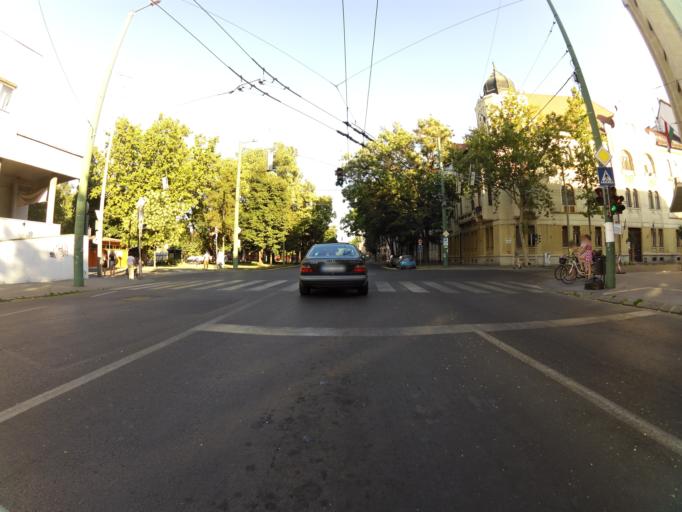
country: HU
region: Csongrad
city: Szeged
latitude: 46.2480
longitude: 20.1458
